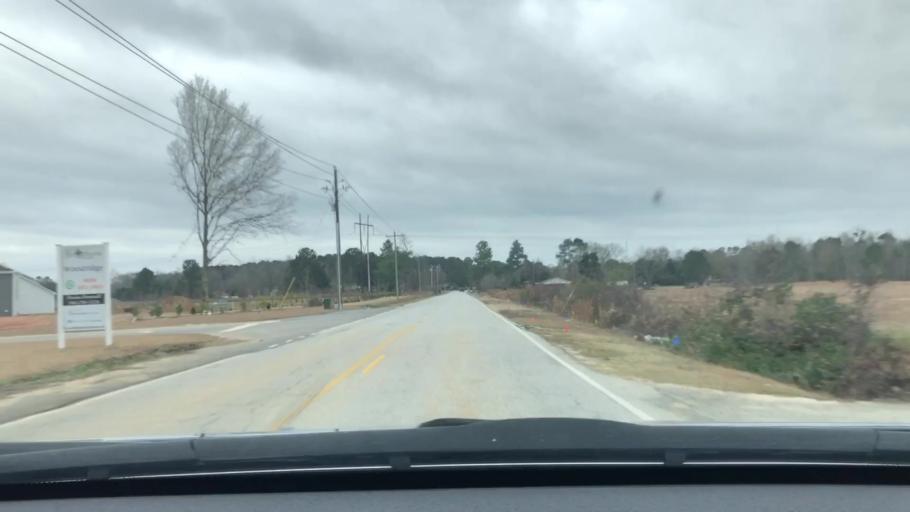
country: US
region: South Carolina
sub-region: Sumter County
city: Cane Savannah
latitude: 33.9231
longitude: -80.4045
